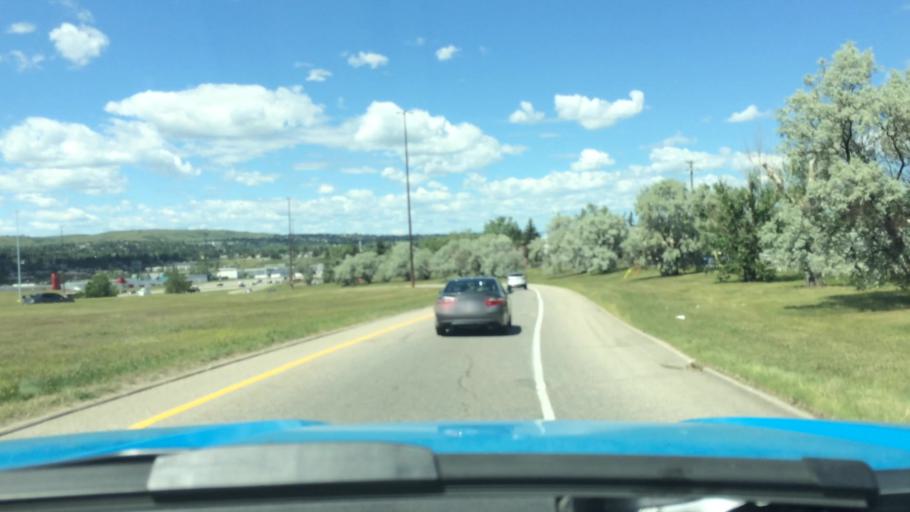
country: CA
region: Alberta
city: Calgary
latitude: 51.0967
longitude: -114.0375
